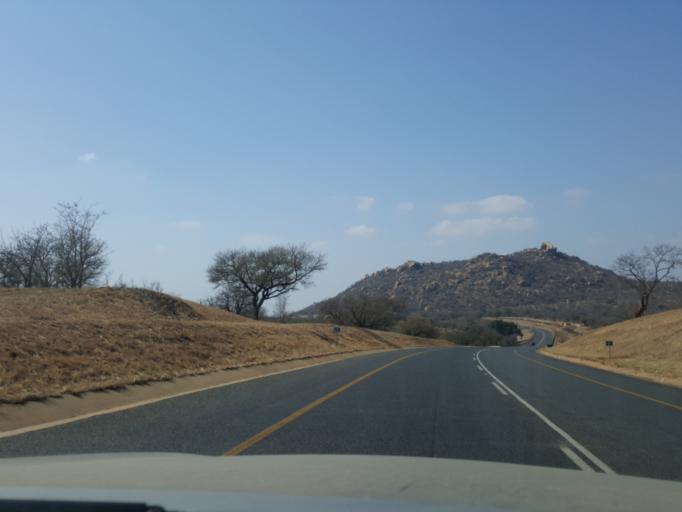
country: ZA
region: Mpumalanga
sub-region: Ehlanzeni District
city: Komatipoort
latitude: -25.4604
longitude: 31.6107
